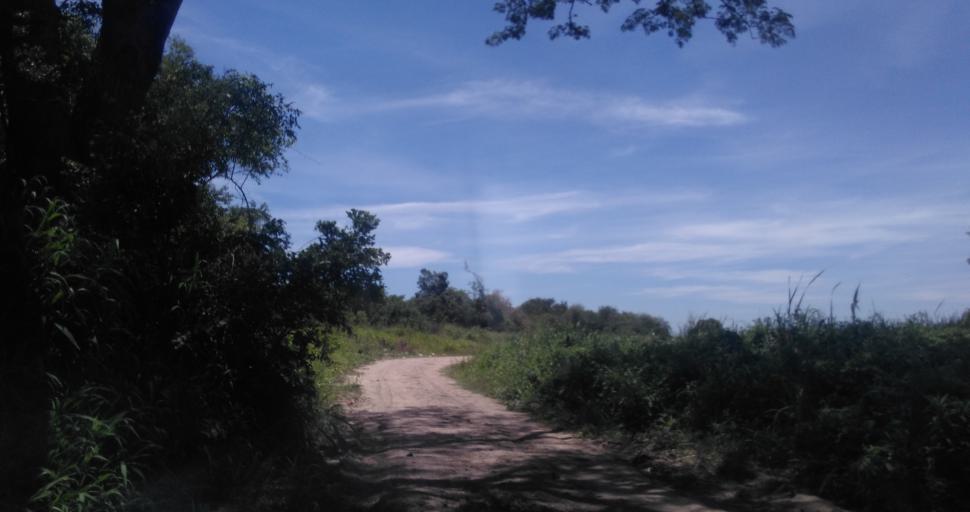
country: AR
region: Chaco
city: Fontana
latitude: -27.4264
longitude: -59.0467
